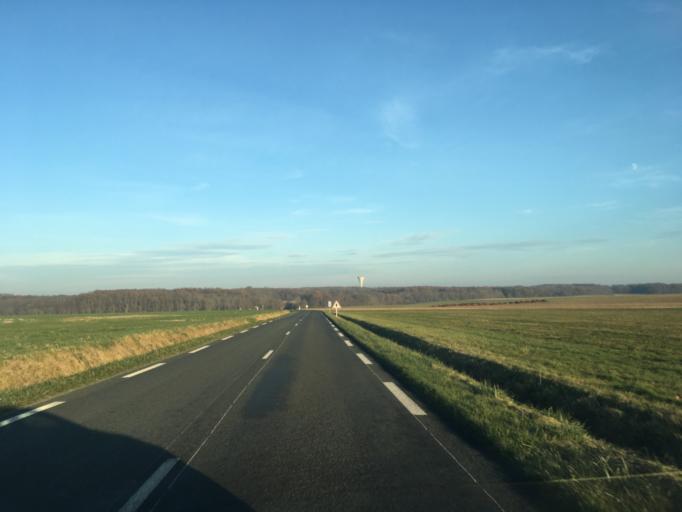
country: FR
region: Haute-Normandie
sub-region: Departement de l'Eure
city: Houlbec-Cocherel
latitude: 49.0608
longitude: 1.3598
